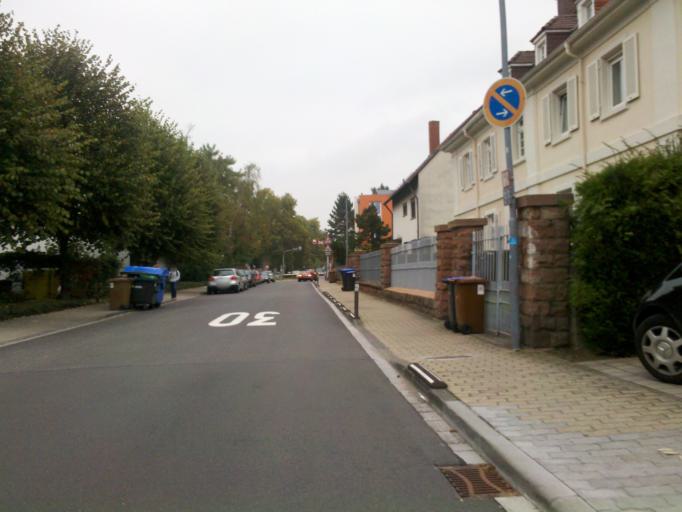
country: DE
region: Baden-Wuerttemberg
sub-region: Karlsruhe Region
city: Eppelheim
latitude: 49.4194
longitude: 8.6476
